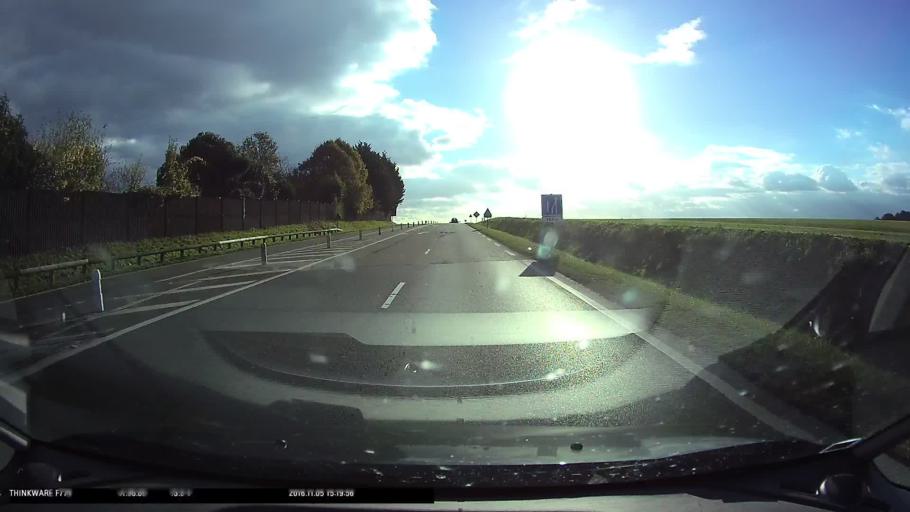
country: FR
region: Ile-de-France
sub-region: Departement du Val-d'Oise
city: Sagy
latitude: 49.0686
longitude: 1.9630
